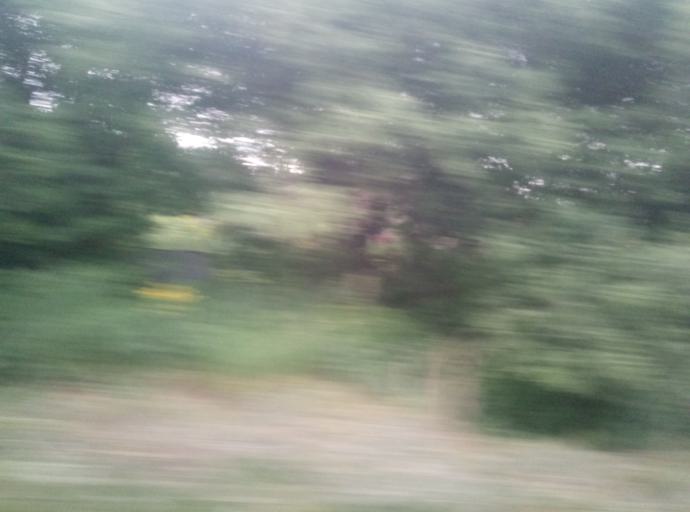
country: RU
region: Tula
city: Kireyevsk
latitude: 53.9669
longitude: 37.9346
